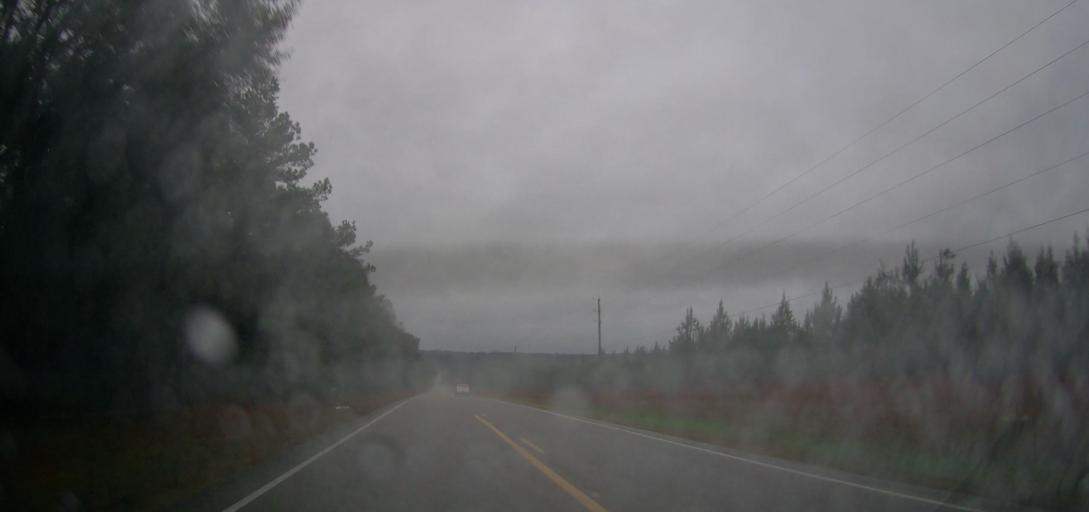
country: US
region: Alabama
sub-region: Autauga County
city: Pine Level
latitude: 32.5443
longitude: -86.6454
